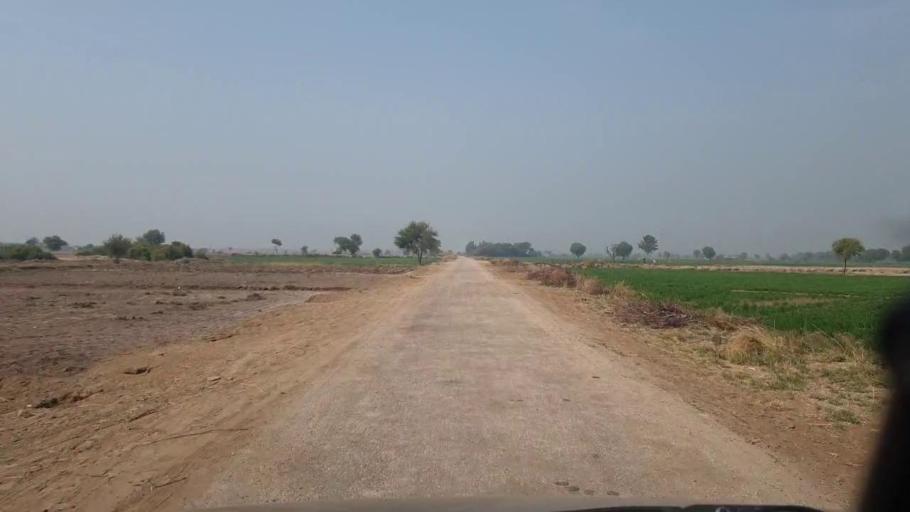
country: PK
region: Sindh
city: Shahdadpur
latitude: 26.0271
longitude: 68.5318
